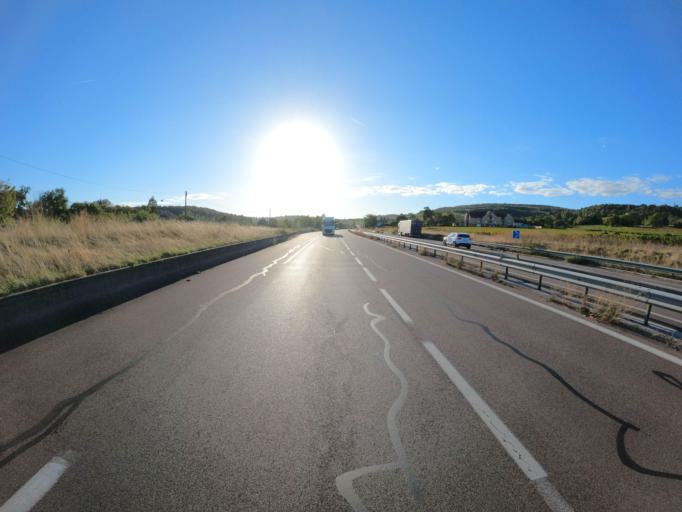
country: FR
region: Bourgogne
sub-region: Departement de Saone-et-Loire
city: Givry
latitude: 46.7568
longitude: 4.7134
